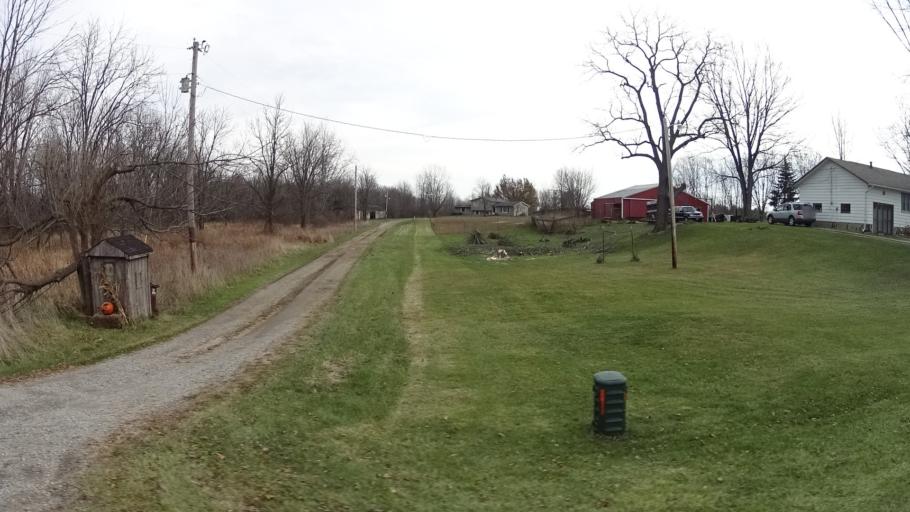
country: US
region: Ohio
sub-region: Lorain County
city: Wellington
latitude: 41.1414
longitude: -82.1698
